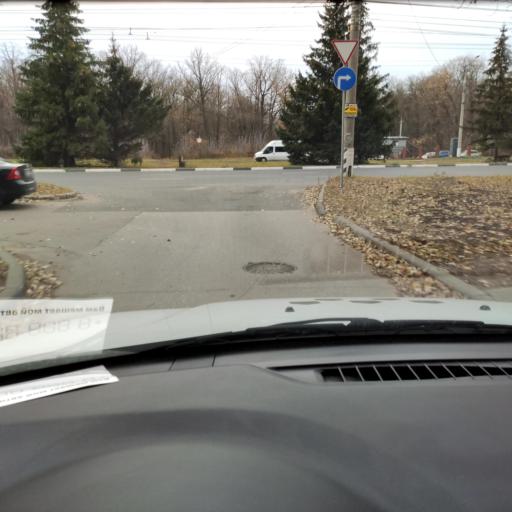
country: RU
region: Samara
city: Tol'yatti
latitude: 53.5062
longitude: 49.4385
